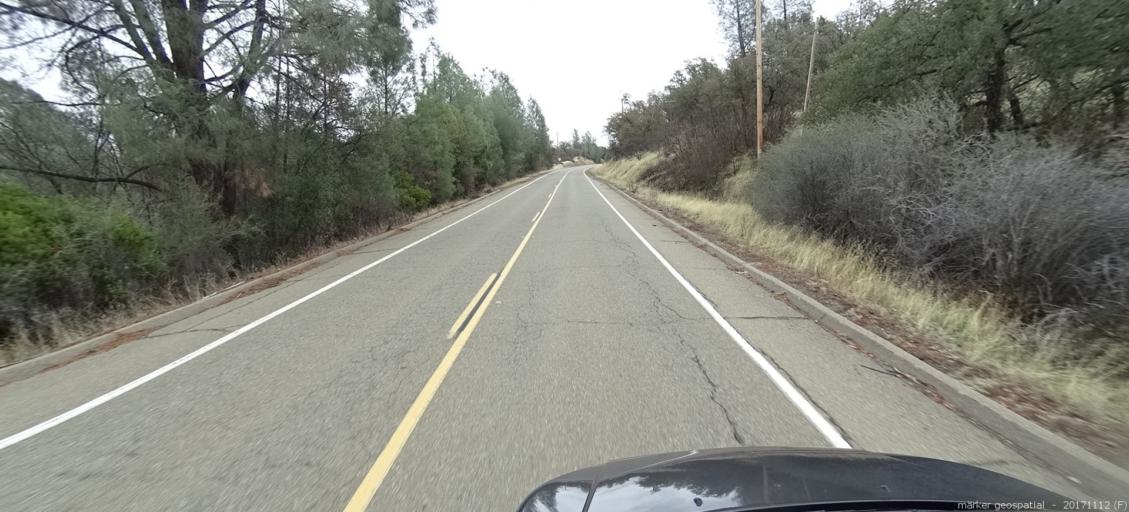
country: US
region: California
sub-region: Shasta County
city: Palo Cedro
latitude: 40.4882
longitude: -122.1342
